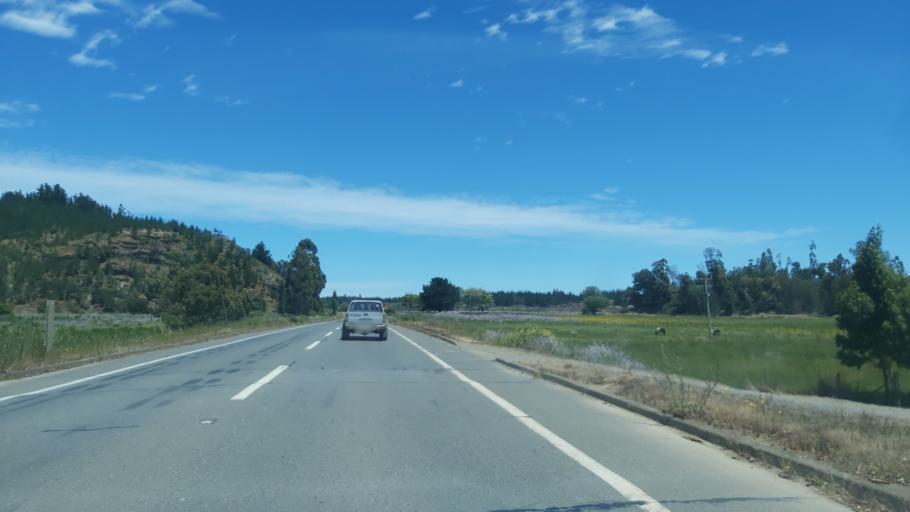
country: CL
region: Maule
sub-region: Provincia de Talca
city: Constitucion
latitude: -35.2793
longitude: -72.3547
